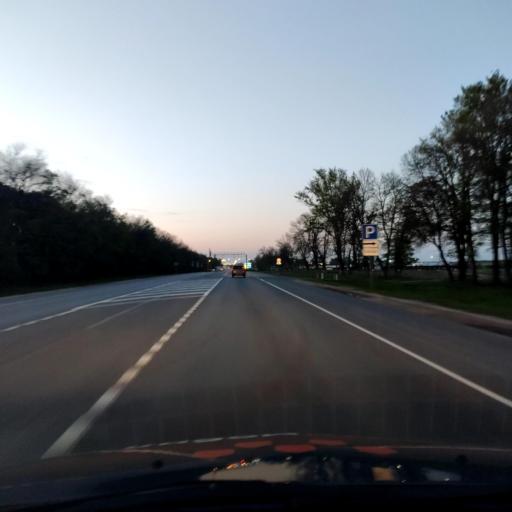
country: RU
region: Orjol
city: Zmiyevka
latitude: 52.7070
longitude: 36.3614
